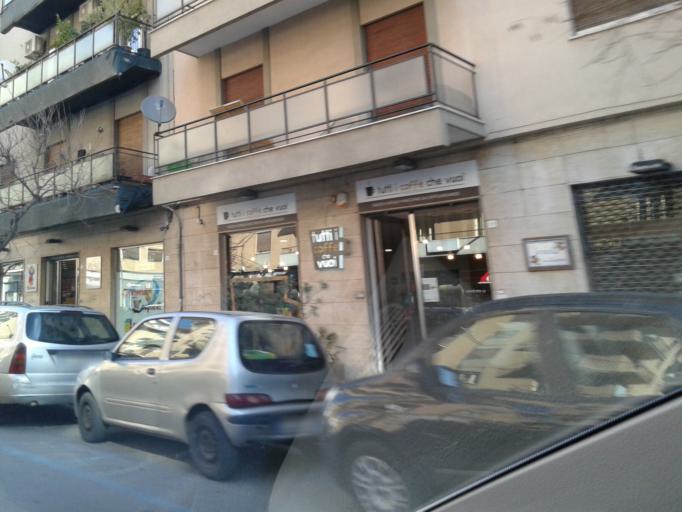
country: IT
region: Sicily
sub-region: Palermo
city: Palermo
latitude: 38.1361
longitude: 13.3447
